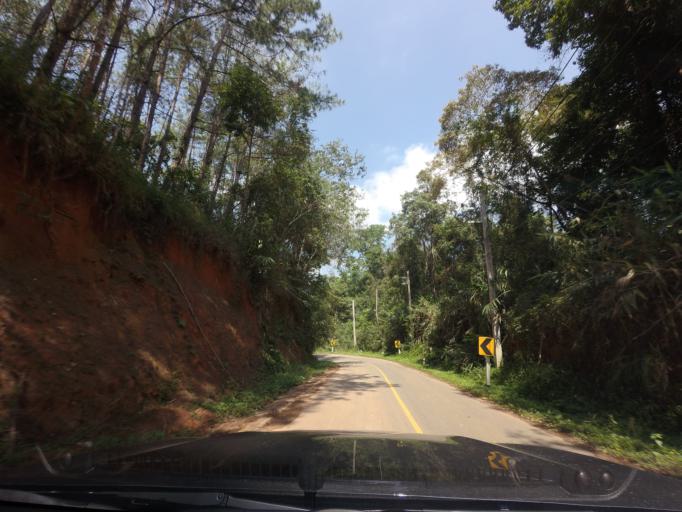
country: TH
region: Loei
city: Na Haeo
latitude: 17.4679
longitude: 100.9251
